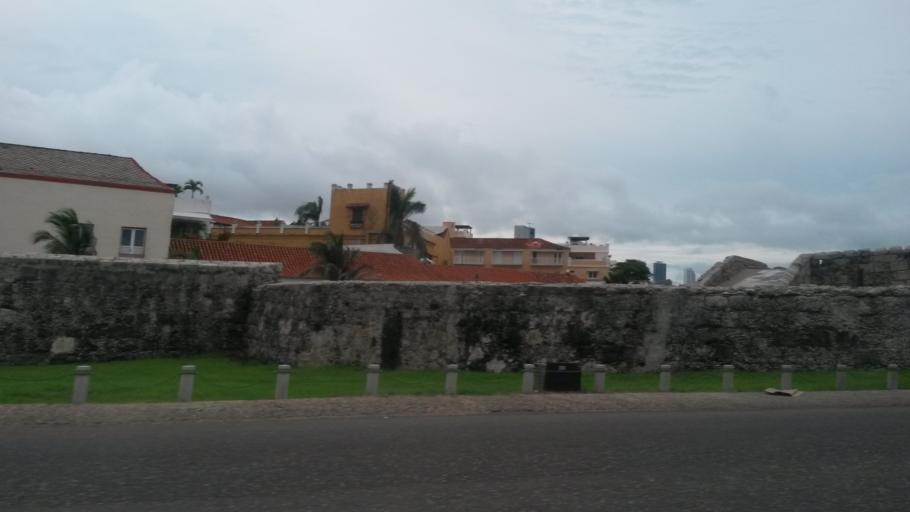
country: CO
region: Bolivar
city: Cartagena
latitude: 10.4259
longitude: -75.5533
